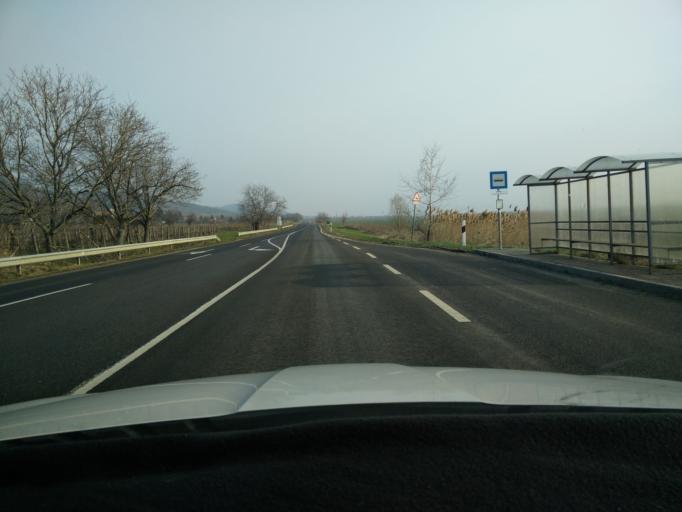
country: HU
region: Tolna
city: Szekszard
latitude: 46.2844
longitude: 18.6846
